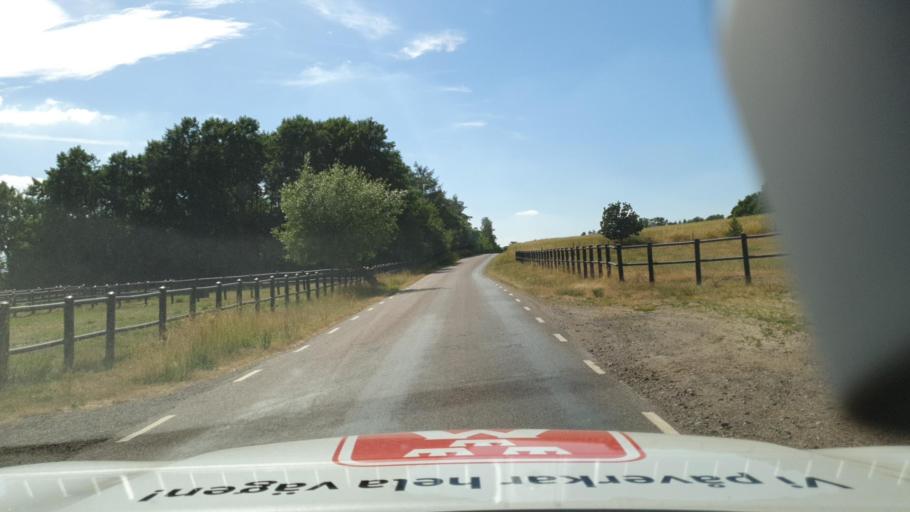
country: SE
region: Skane
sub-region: Sjobo Kommun
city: Blentarp
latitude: 55.6051
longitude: 13.5998
